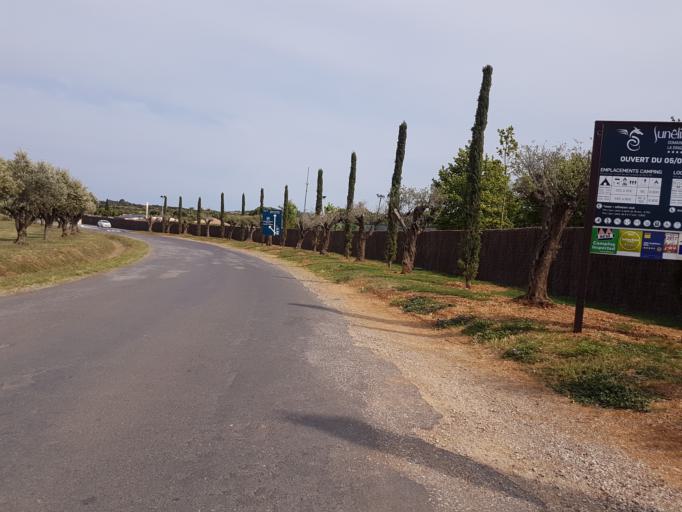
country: FR
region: Languedoc-Roussillon
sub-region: Departement de l'Herault
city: Portiragnes
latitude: 43.3132
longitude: 3.3609
